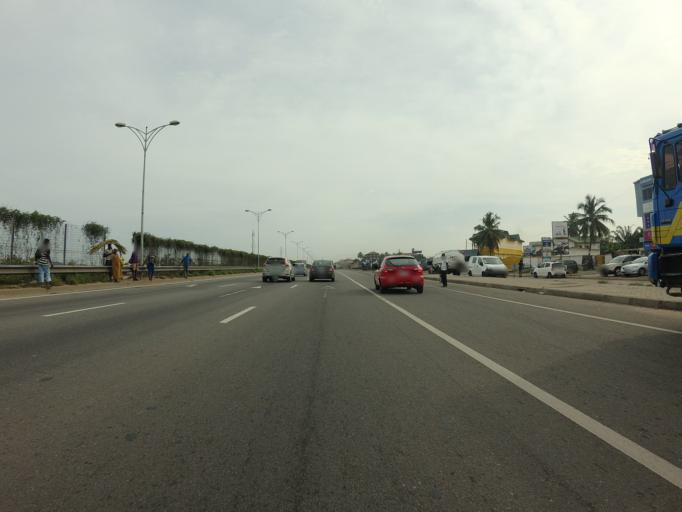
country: GH
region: Greater Accra
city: Gbawe
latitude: 5.5798
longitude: -0.2776
